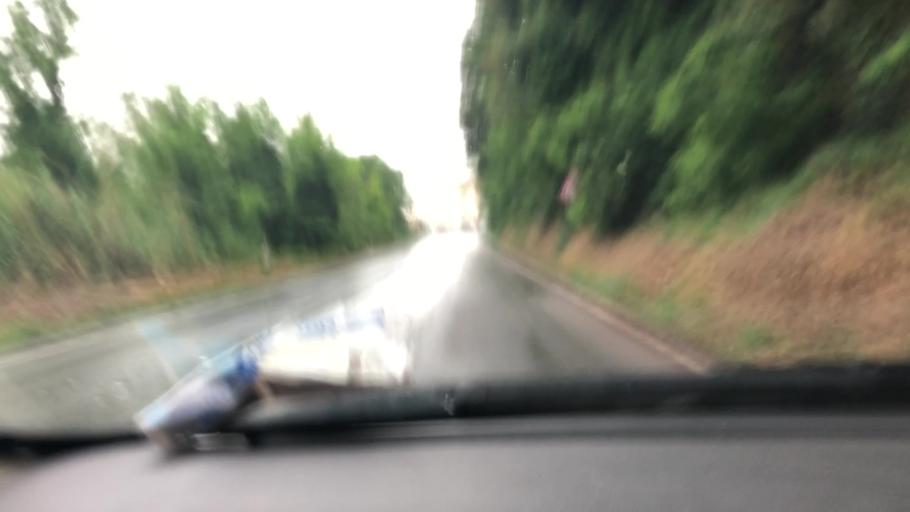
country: IT
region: Tuscany
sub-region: Province of Pisa
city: Pontedera
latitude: 43.6795
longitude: 10.6417
